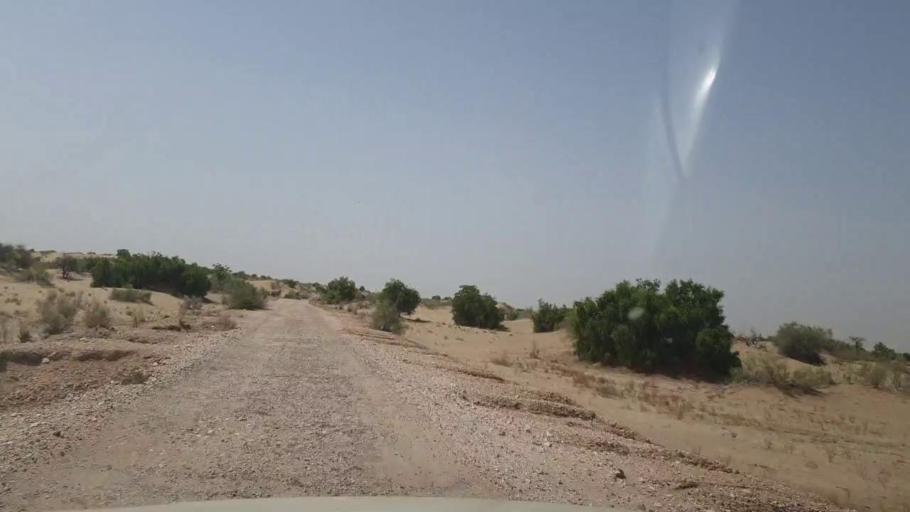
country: PK
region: Sindh
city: Khanpur
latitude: 27.4120
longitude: 69.3194
